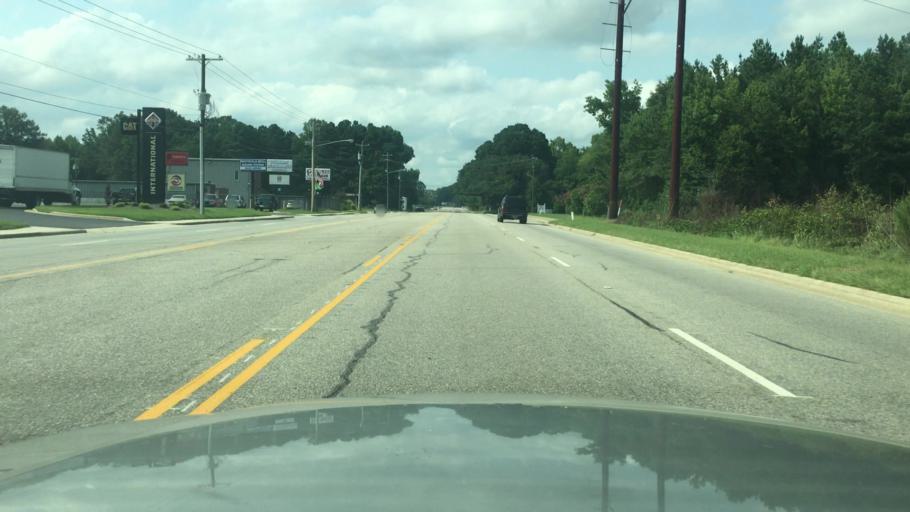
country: US
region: North Carolina
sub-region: Cumberland County
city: Fayetteville
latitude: 35.0289
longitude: -78.8437
